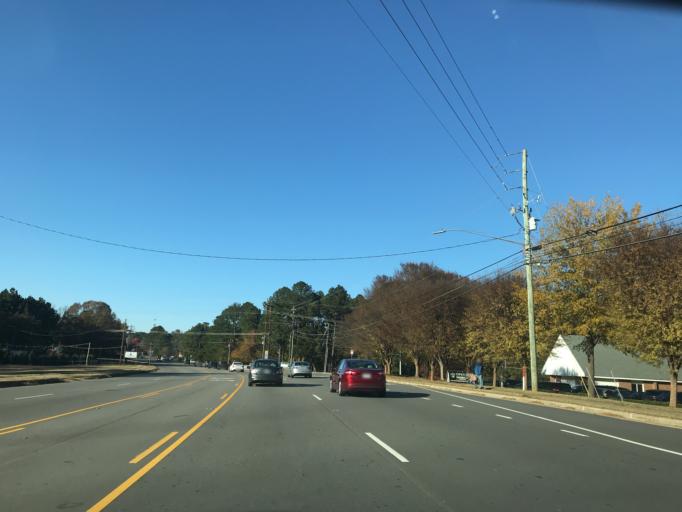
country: US
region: North Carolina
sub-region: Wake County
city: West Raleigh
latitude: 35.8567
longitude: -78.6158
